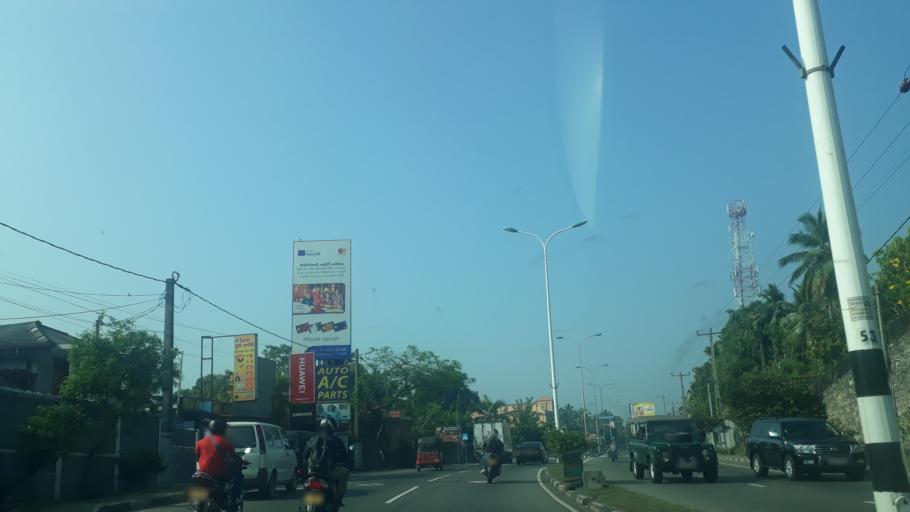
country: LK
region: Western
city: Kelaniya
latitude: 6.9968
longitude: 79.9479
